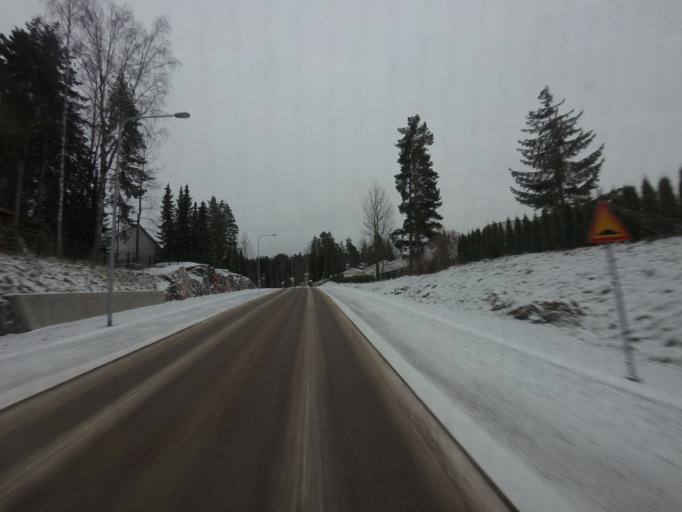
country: FI
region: Uusimaa
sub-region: Helsinki
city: Espoo
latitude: 60.1984
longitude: 24.6864
